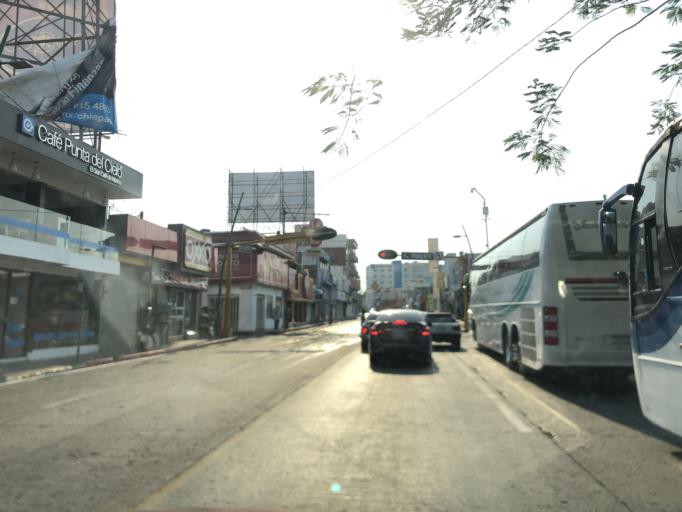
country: MX
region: Chiapas
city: Tuxtla Gutierrez
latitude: 16.7548
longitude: -93.1236
